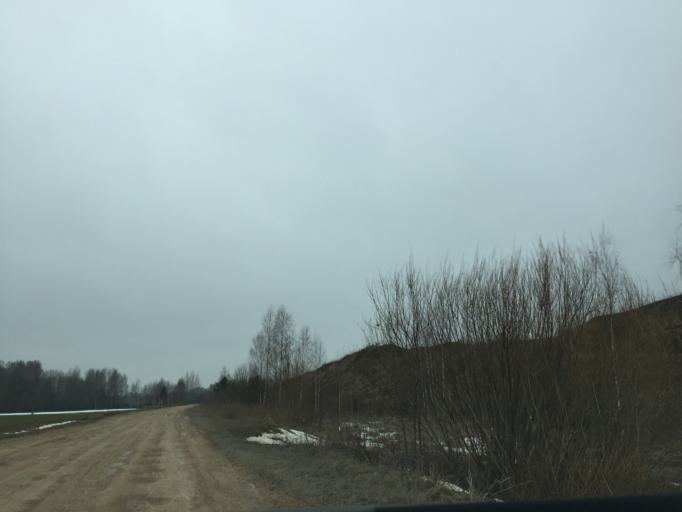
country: LV
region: Lecava
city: Iecava
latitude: 56.5721
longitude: 24.0617
